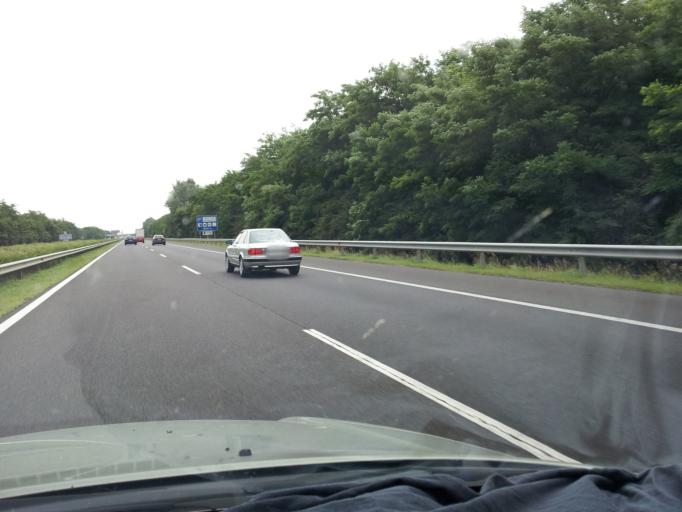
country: HU
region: Heves
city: Kal
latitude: 47.7224
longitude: 20.2933
